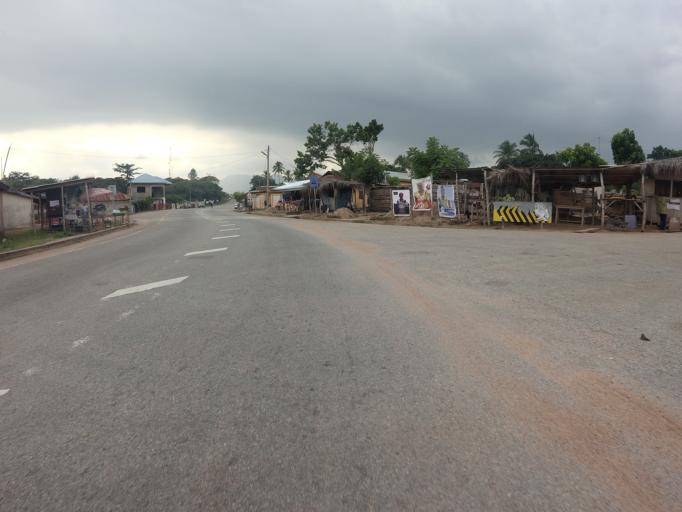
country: GH
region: Volta
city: Ho
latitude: 6.7706
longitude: 0.4810
